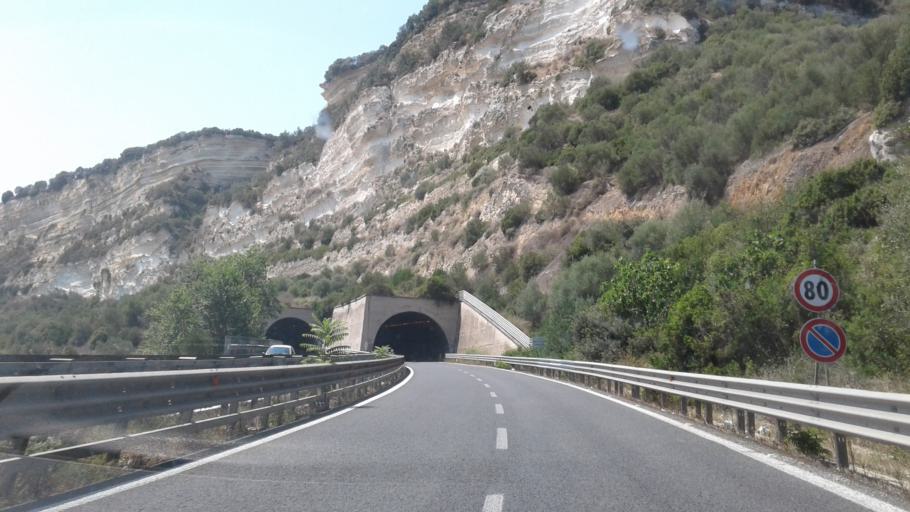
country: IT
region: Sardinia
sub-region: Provincia di Sassari
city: Ossi
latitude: 40.7010
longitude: 8.5898
